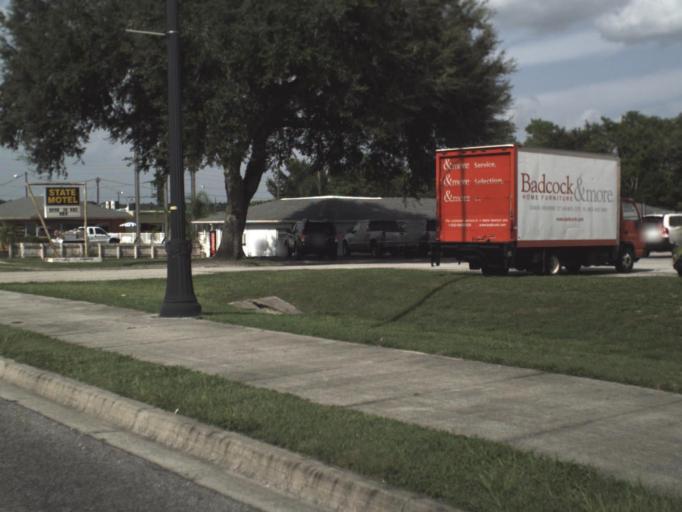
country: US
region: Florida
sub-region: Polk County
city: Haines City
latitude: 28.1154
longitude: -81.6397
